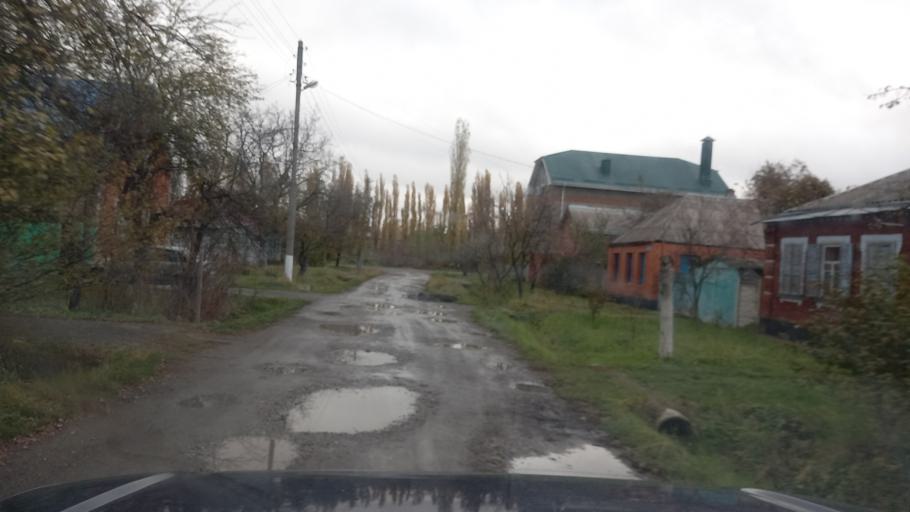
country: RU
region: Adygeya
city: Maykop
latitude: 44.6195
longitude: 40.1289
